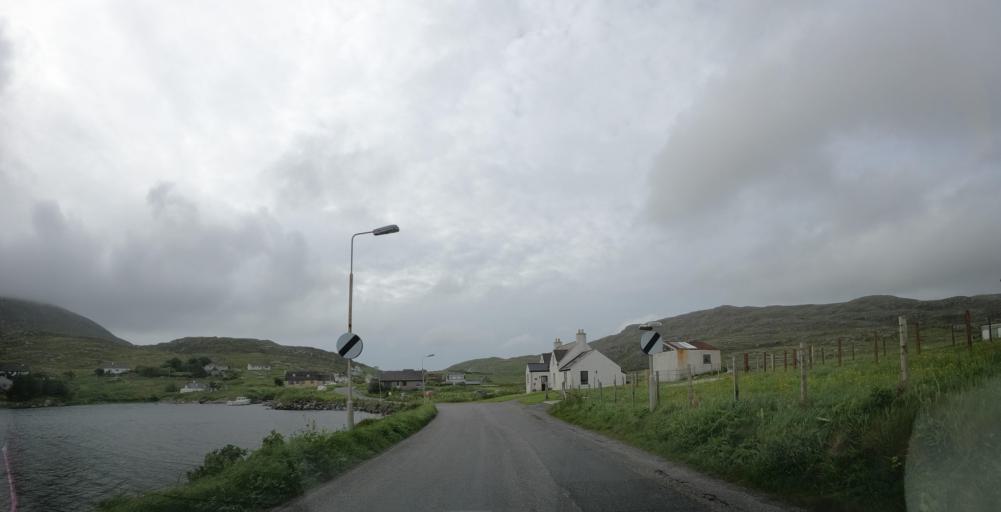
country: GB
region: Scotland
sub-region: Eilean Siar
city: Barra
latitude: 56.9573
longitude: -7.5018
